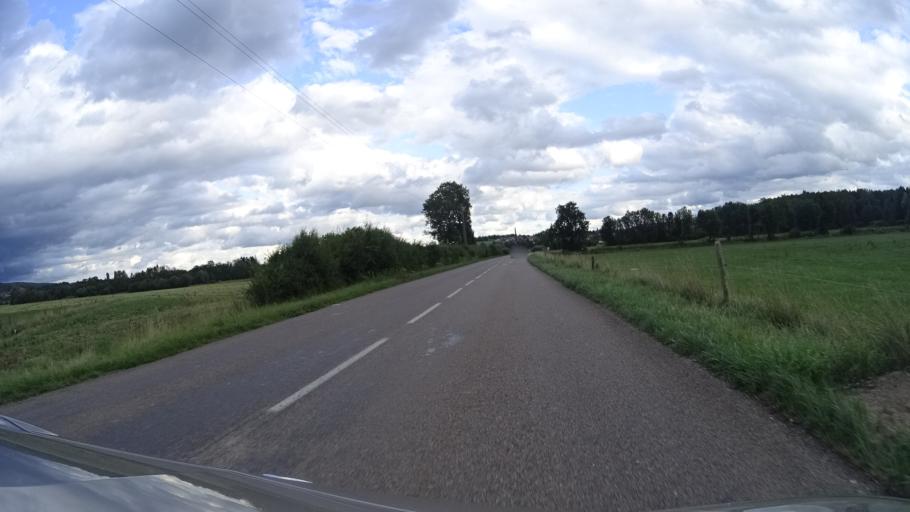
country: FR
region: Franche-Comte
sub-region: Departement du Doubs
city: Saone
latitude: 47.2331
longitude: 6.1057
